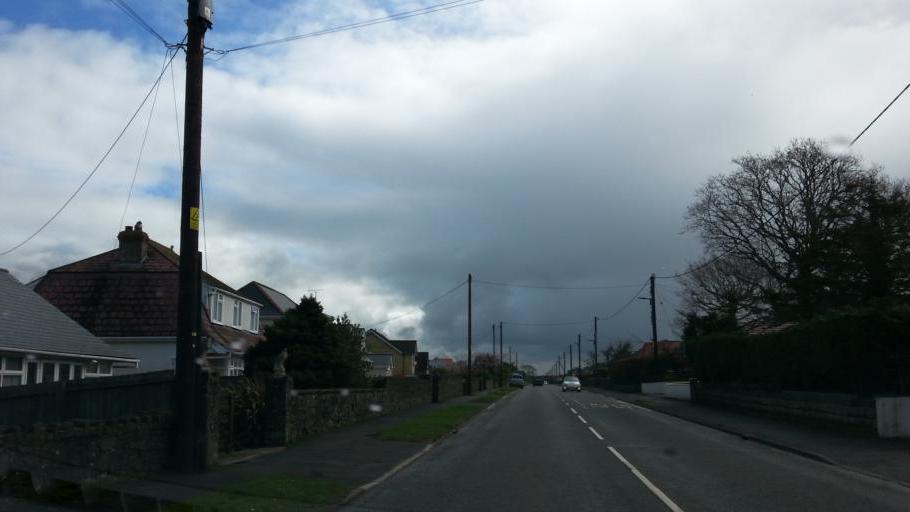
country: GB
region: England
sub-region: Devon
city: Fremington
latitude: 51.0700
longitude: -4.1448
